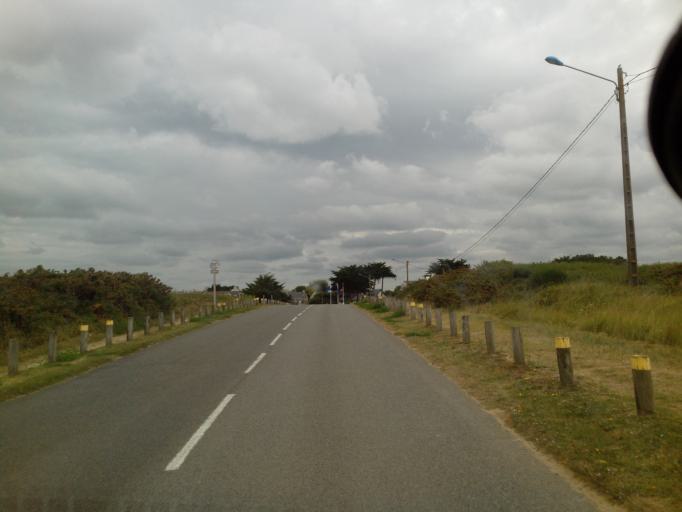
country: FR
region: Brittany
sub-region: Departement du Morbihan
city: Erdeven
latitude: 47.6144
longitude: -3.1667
